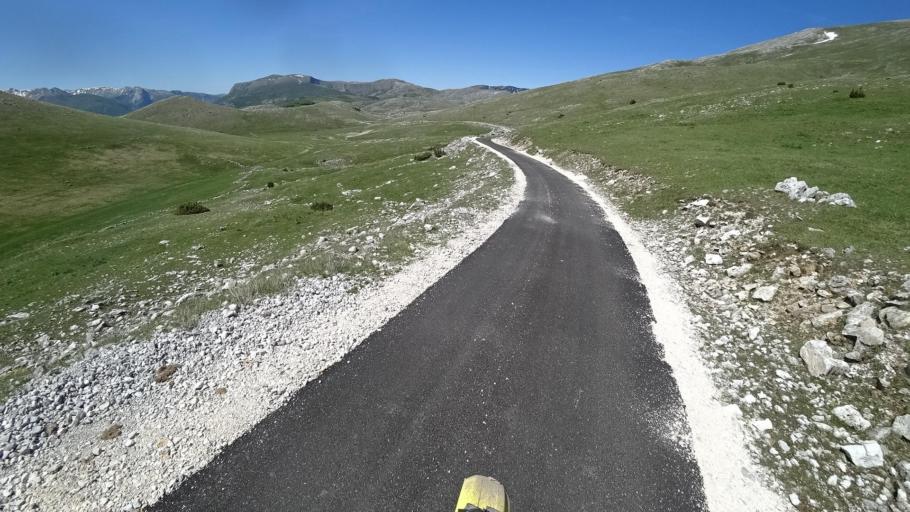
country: BA
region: Federation of Bosnia and Herzegovina
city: Gracanica
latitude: 43.6920
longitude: 18.2634
